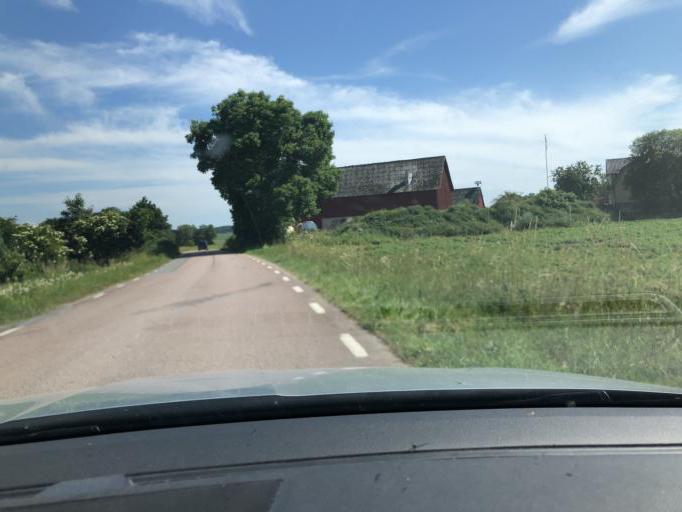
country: SE
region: Blekinge
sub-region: Solvesborgs Kommun
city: Soelvesborg
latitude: 56.1204
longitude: 14.6185
